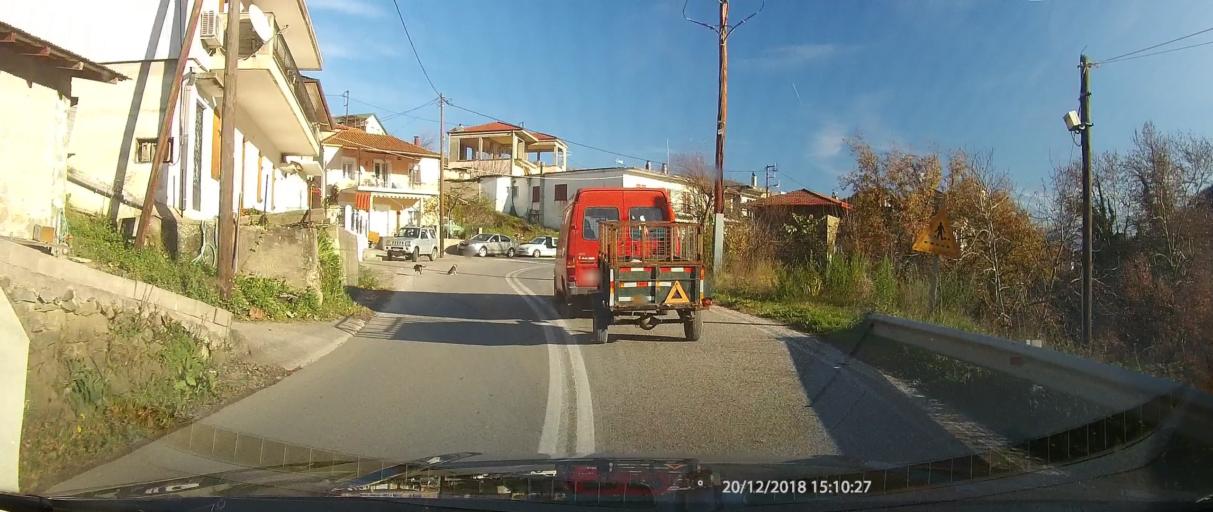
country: GR
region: Central Greece
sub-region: Nomos Fthiotidos
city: Makrakomi
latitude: 38.9476
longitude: 21.9522
